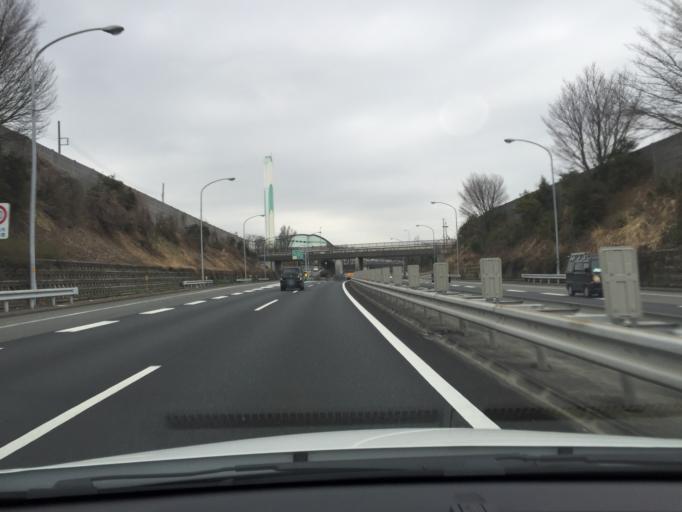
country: JP
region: Saitama
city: Sayama
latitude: 35.8202
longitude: 139.3710
